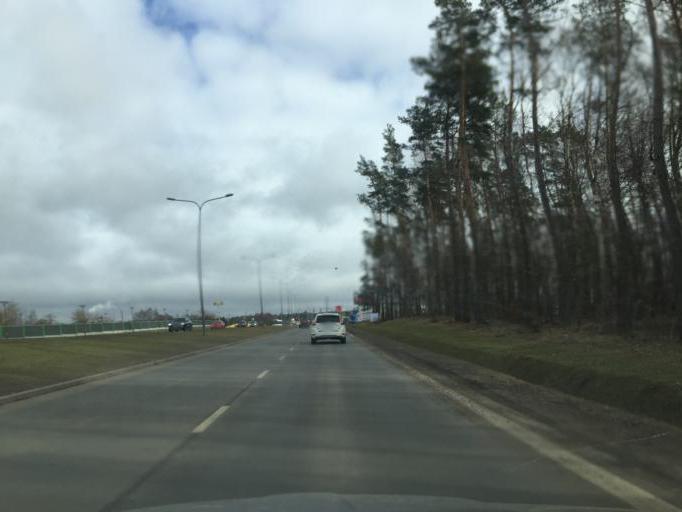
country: PL
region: Pomeranian Voivodeship
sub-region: Sopot
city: Sopot
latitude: 54.3770
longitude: 18.5044
